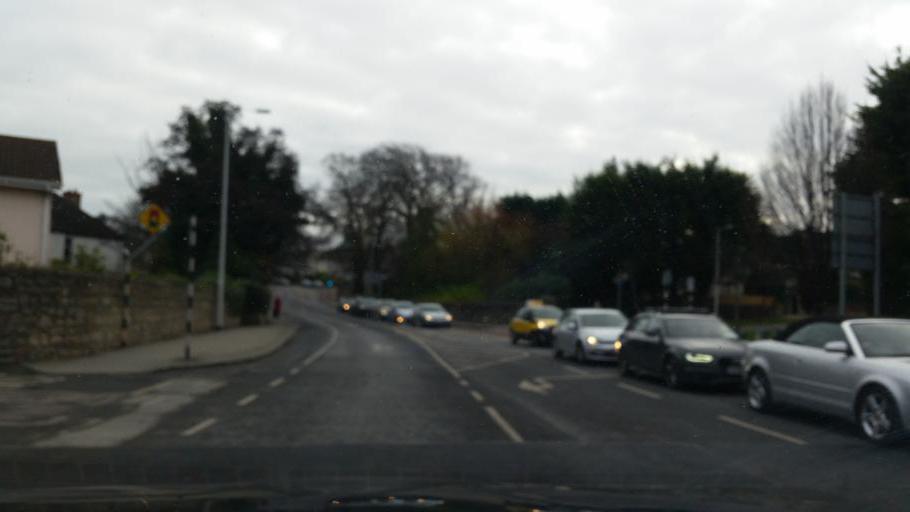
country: IE
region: Leinster
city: Balally
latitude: 53.2854
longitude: -6.2380
